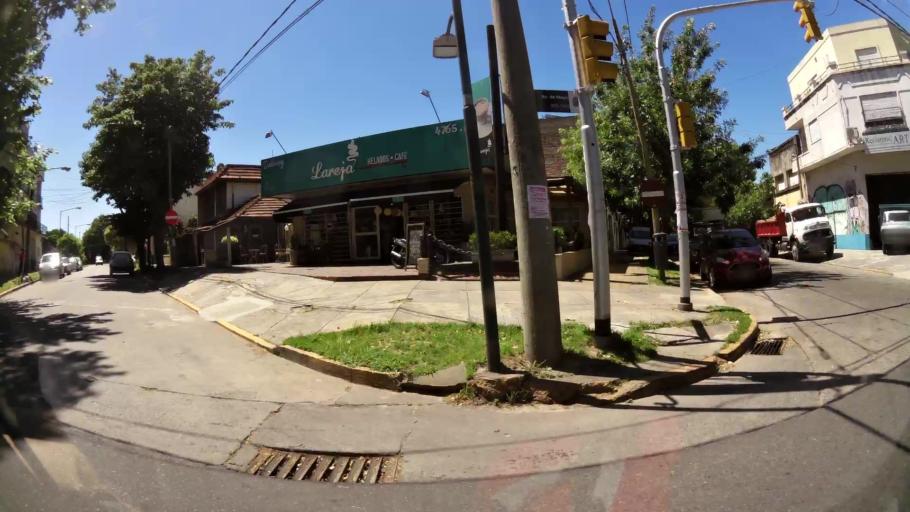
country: AR
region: Buenos Aires
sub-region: Partido de General San Martin
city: General San Martin
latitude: -34.5182
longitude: -58.5436
